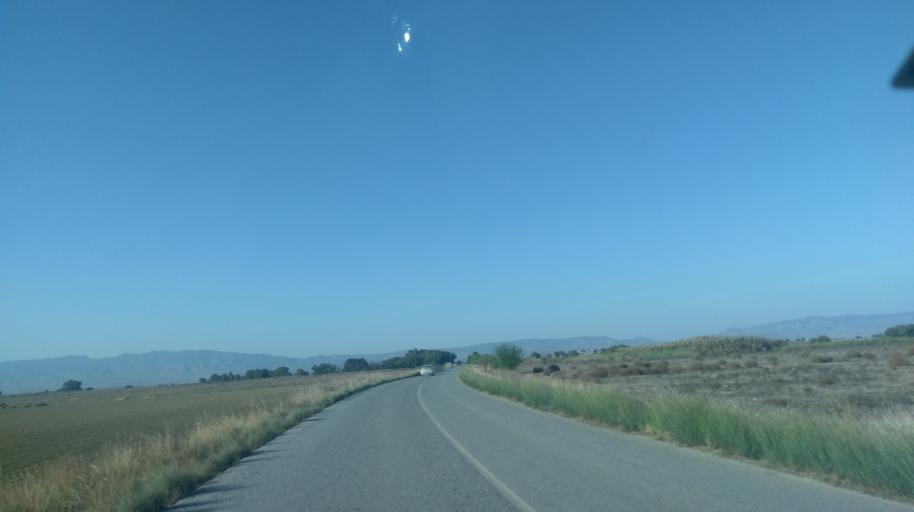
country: CY
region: Ammochostos
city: Lefkonoiko
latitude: 35.1950
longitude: 33.6962
